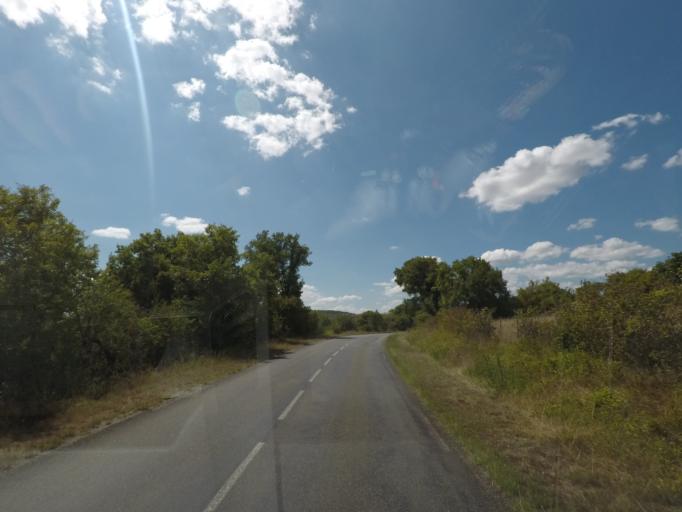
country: FR
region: Midi-Pyrenees
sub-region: Departement du Lot
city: Lacapelle-Marival
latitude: 44.6258
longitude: 1.8740
